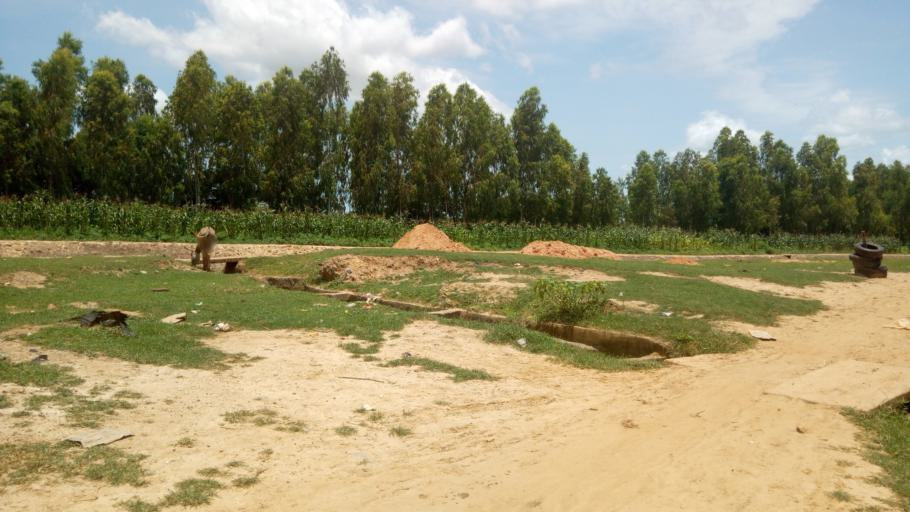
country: ML
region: Sikasso
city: Koutiala
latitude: 12.3898
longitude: -5.4602
